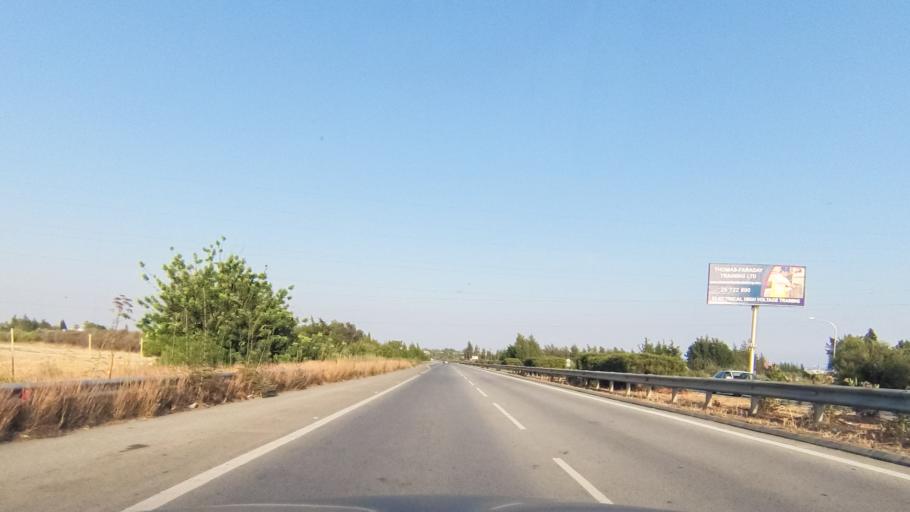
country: CY
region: Limassol
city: Ypsonas
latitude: 34.6904
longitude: 32.9804
